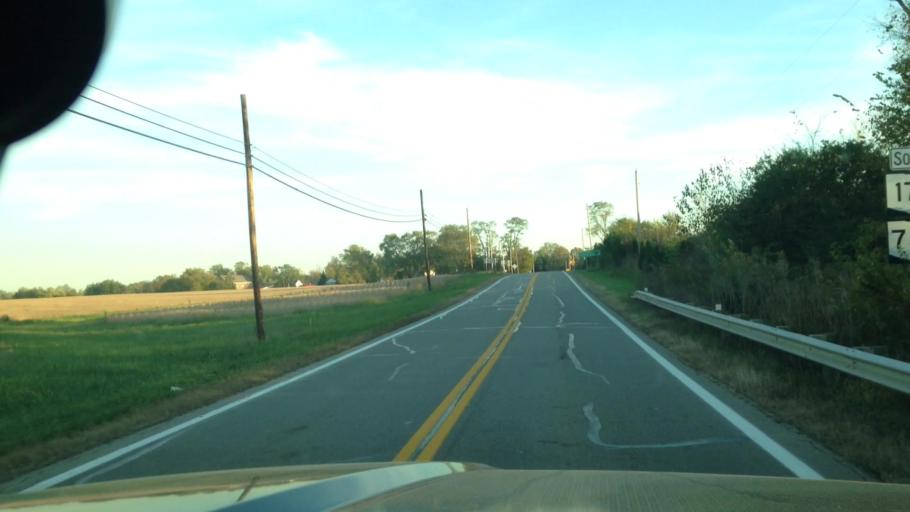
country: US
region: Ohio
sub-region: Butler County
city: Oxford
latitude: 39.5997
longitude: -84.7415
